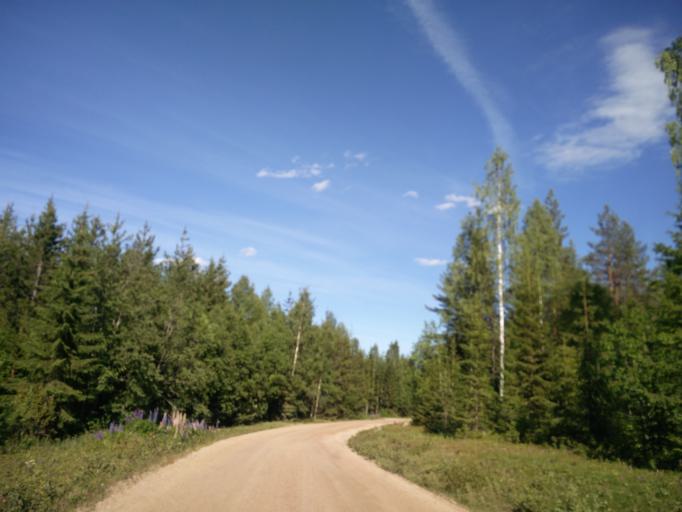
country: SE
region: Gaevleborg
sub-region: Hudiksvalls Kommun
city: Delsbo
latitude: 62.1867
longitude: 16.4519
